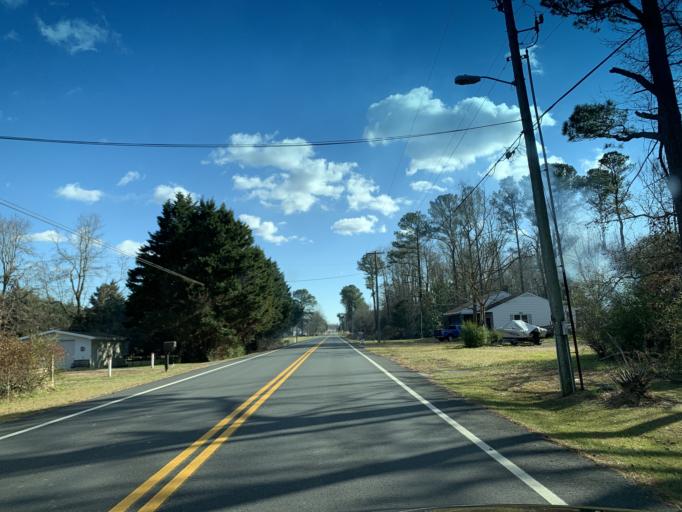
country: US
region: Maryland
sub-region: Worcester County
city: Berlin
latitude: 38.3590
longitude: -75.1987
